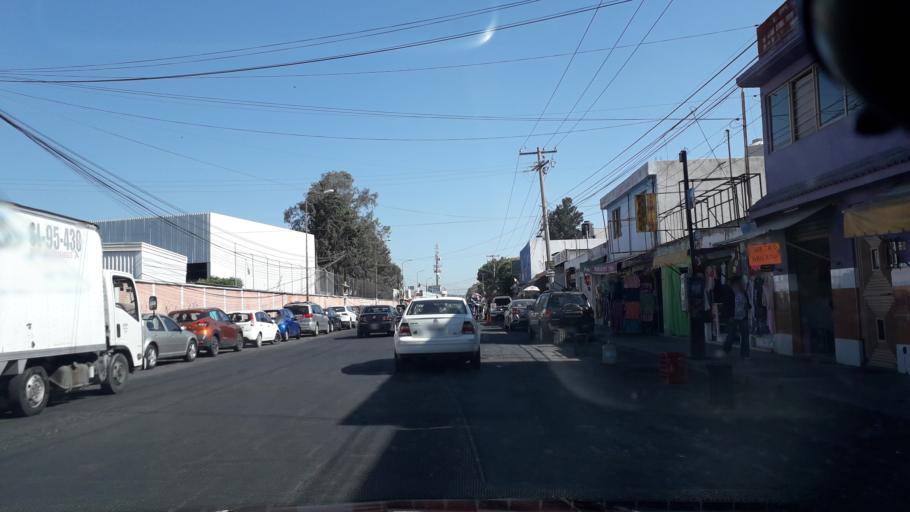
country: MX
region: Puebla
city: Puebla
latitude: 19.0729
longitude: -98.2109
